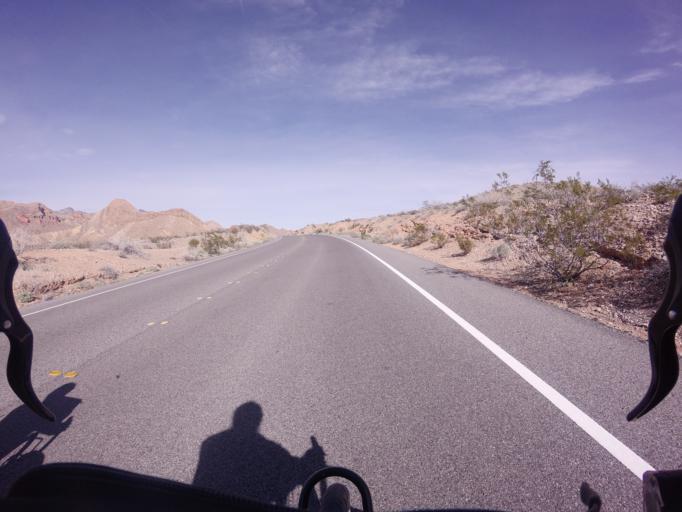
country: US
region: Nevada
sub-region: Clark County
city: Boulder City
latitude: 36.2024
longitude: -114.6690
